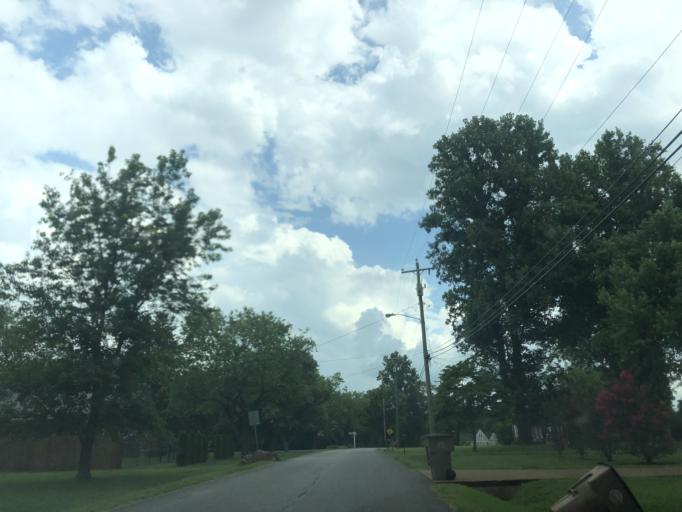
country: US
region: Tennessee
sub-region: Davidson County
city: Lakewood
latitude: 36.1657
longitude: -86.6691
